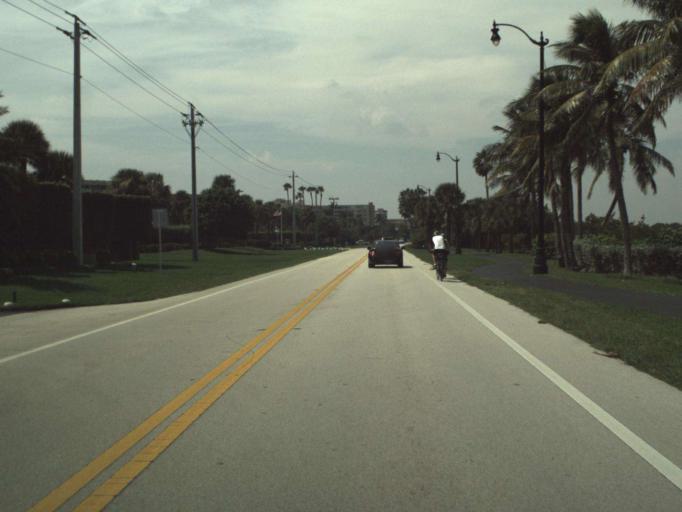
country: US
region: Florida
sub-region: Palm Beach County
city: South Palm Beach
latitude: 26.6018
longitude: -80.0386
